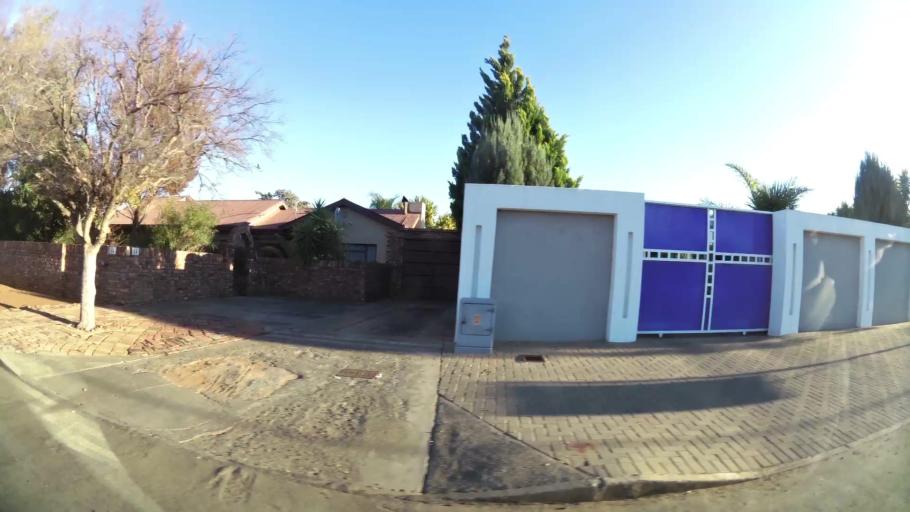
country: ZA
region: Northern Cape
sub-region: Frances Baard District Municipality
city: Kimberley
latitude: -28.7585
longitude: 24.7474
